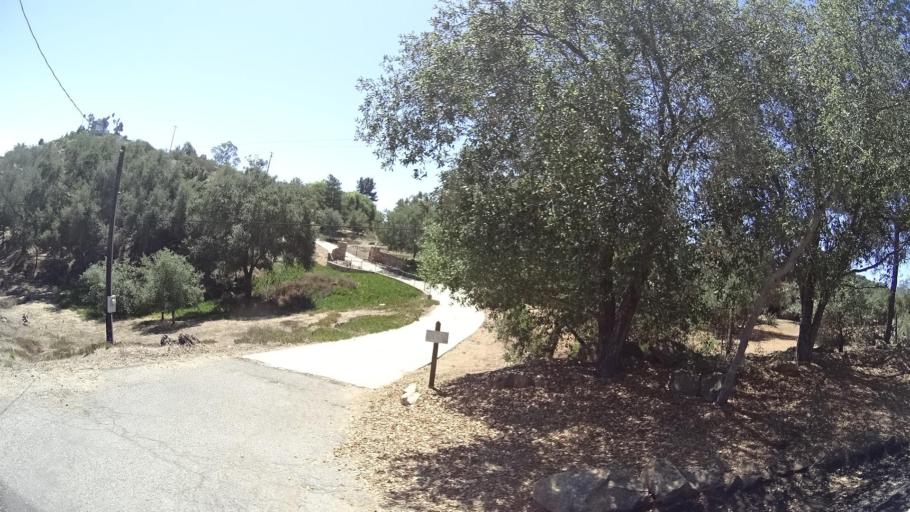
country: US
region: California
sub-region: San Diego County
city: Rainbow
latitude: 33.3845
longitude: -117.1237
